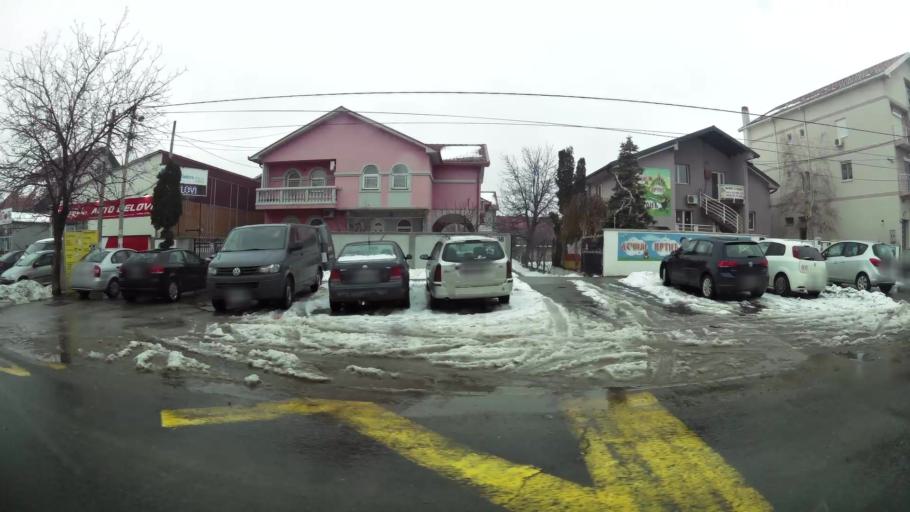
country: RS
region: Central Serbia
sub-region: Belgrade
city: Zemun
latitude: 44.8471
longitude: 20.3657
